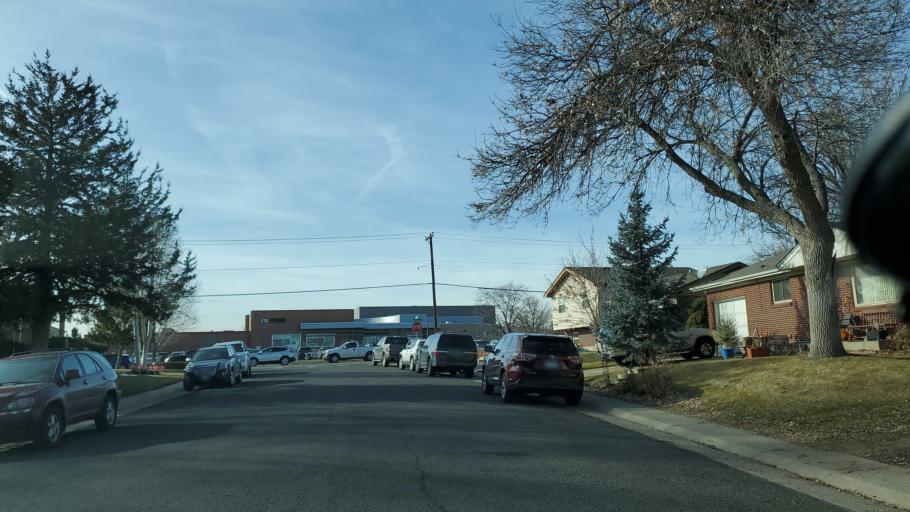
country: US
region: Colorado
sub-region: Adams County
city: Northglenn
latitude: 39.9064
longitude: -104.9643
